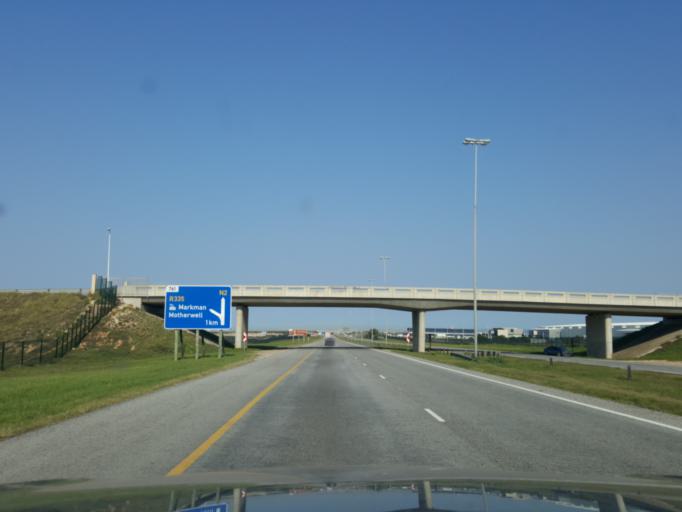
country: ZA
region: Eastern Cape
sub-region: Nelson Mandela Bay Metropolitan Municipality
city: Port Elizabeth
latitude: -33.8117
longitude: 25.6517
